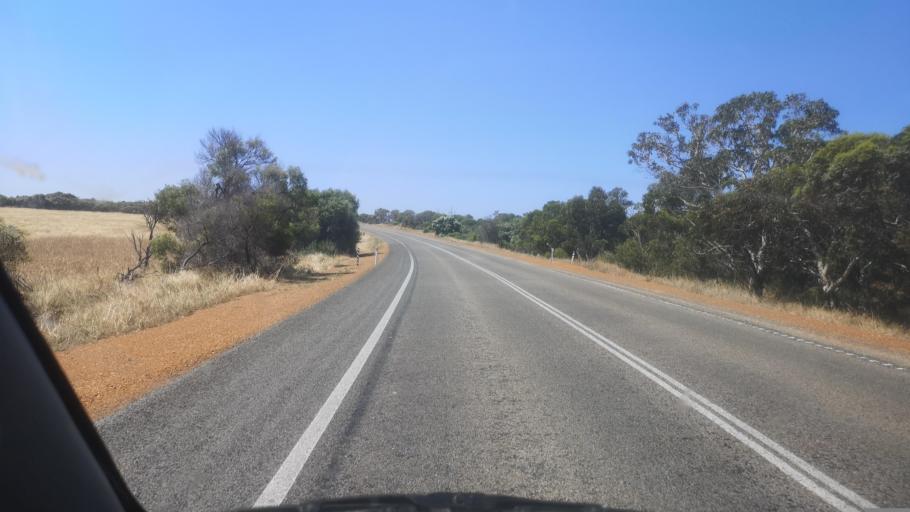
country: AU
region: Western Australia
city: Port Denison
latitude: -29.3562
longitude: 115.0124
